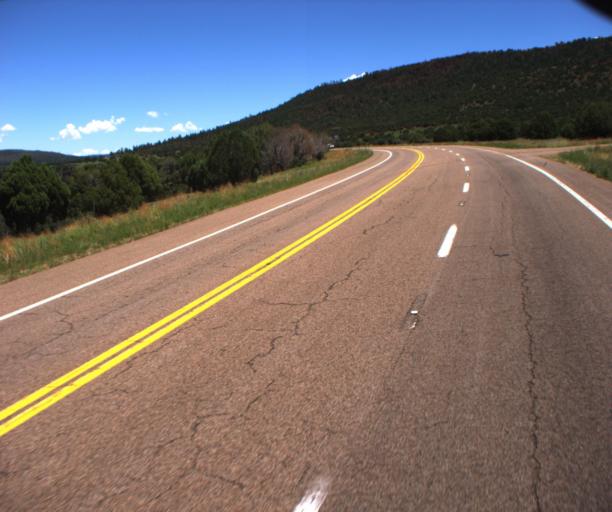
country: US
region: Arizona
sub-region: Navajo County
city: Cibecue
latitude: 34.0397
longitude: -110.2306
